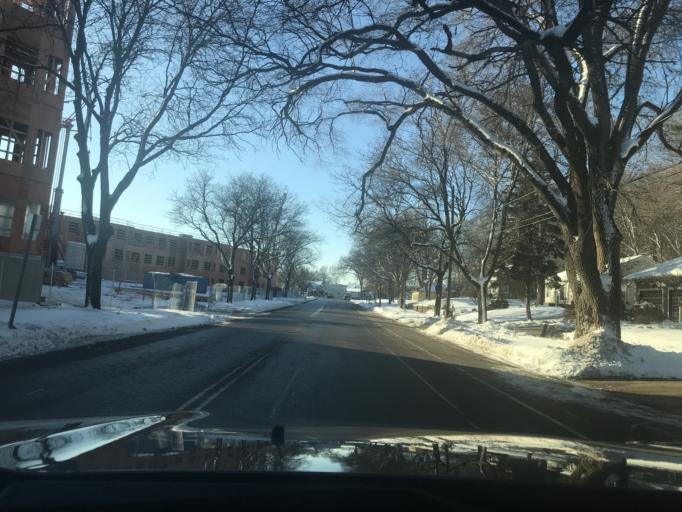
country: US
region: Minnesota
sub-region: Dakota County
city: Mendota Heights
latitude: 44.9144
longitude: -93.1487
